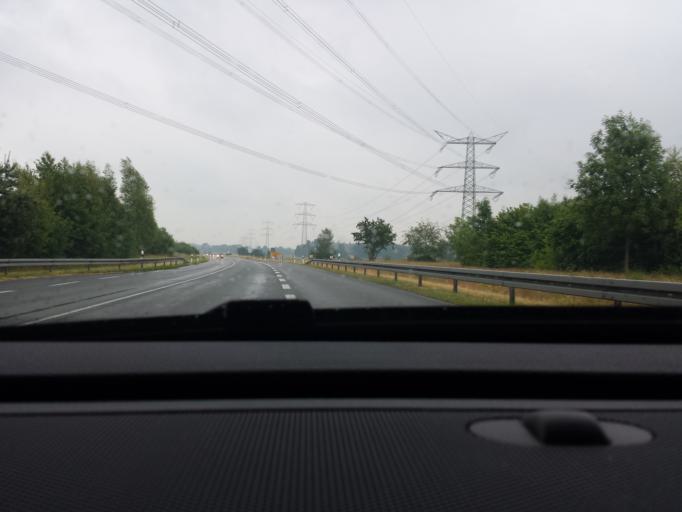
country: DE
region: North Rhine-Westphalia
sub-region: Regierungsbezirk Munster
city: Gronau
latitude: 52.1916
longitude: 6.9754
